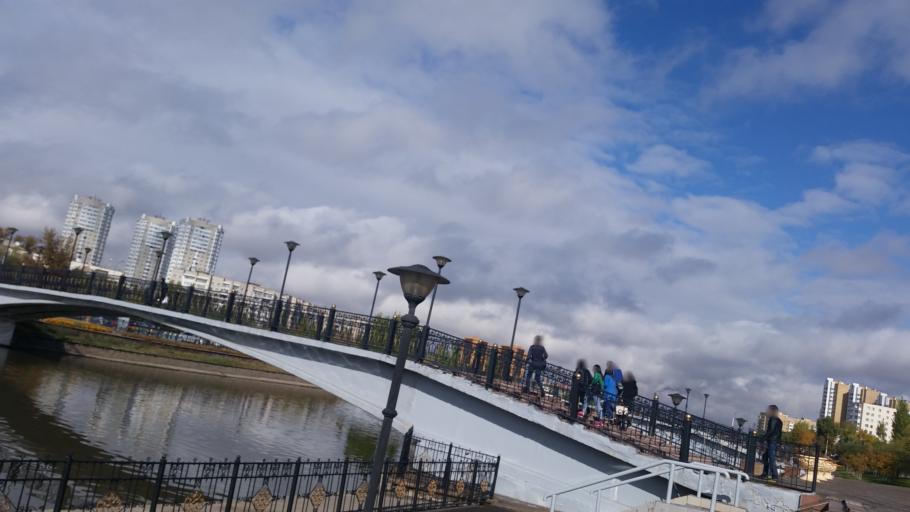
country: KZ
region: Astana Qalasy
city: Astana
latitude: 51.1586
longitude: 71.4666
